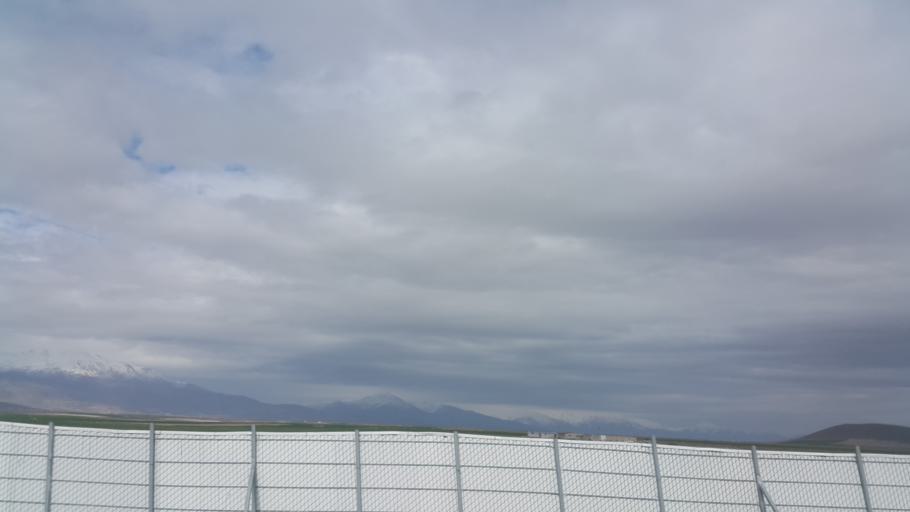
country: TR
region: Aksaray
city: Taspinar
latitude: 37.9888
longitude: 34.0680
